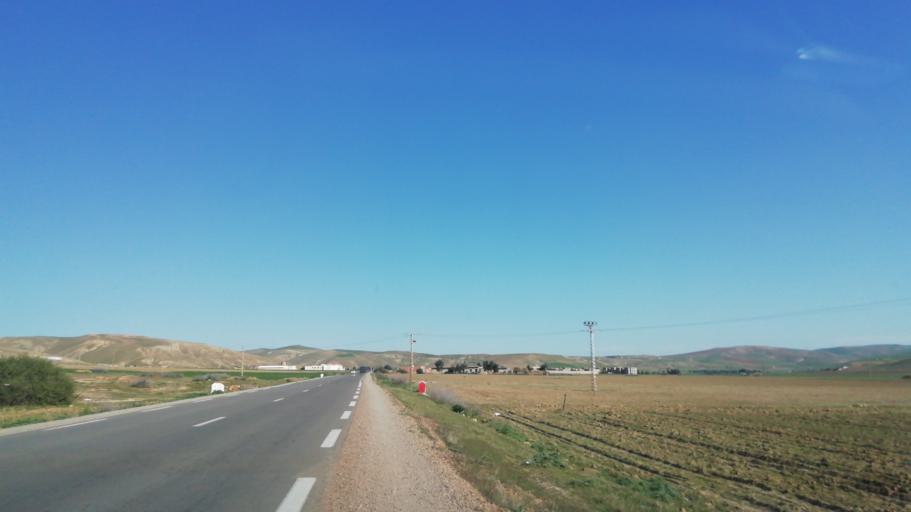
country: DZ
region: Mascara
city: Oued el Abtal
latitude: 35.4448
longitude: 0.8355
